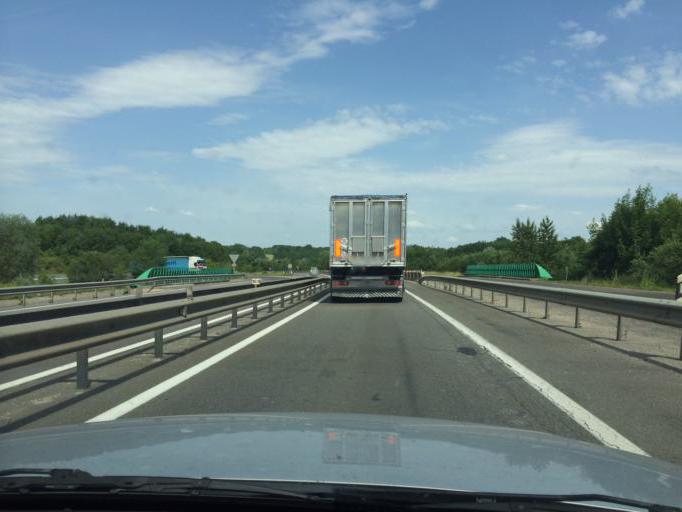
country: FR
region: Champagne-Ardenne
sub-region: Departement de la Haute-Marne
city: Bettancourt-la-Ferree
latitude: 48.6205
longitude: 4.9826
